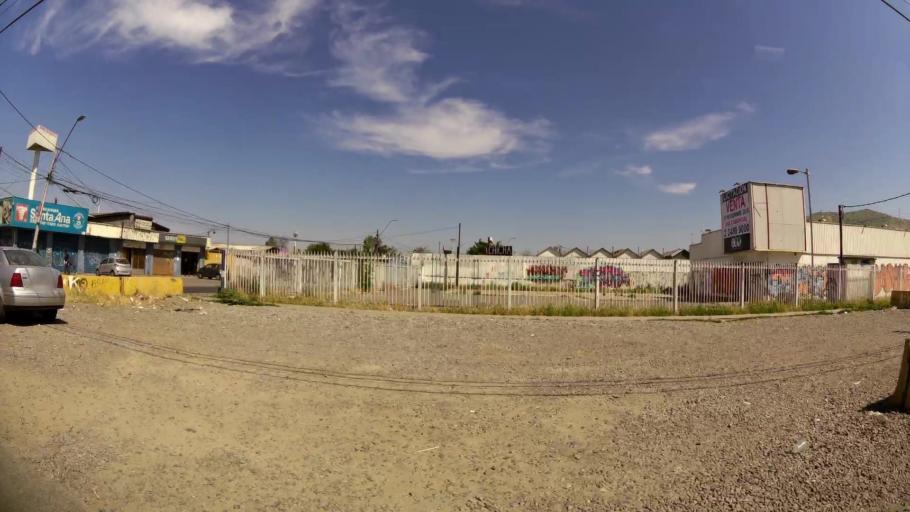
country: CL
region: Santiago Metropolitan
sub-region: Provincia de Santiago
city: Lo Prado
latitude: -33.4006
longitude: -70.7212
